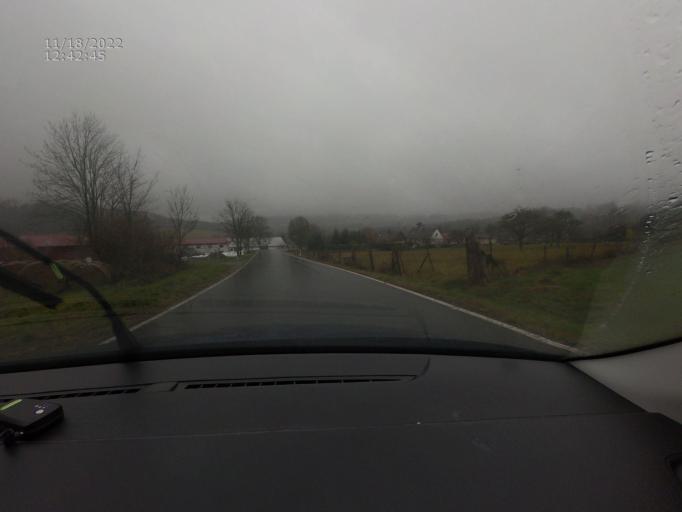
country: CZ
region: Plzensky
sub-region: Okres Klatovy
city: Planice
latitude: 49.3723
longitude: 13.4509
